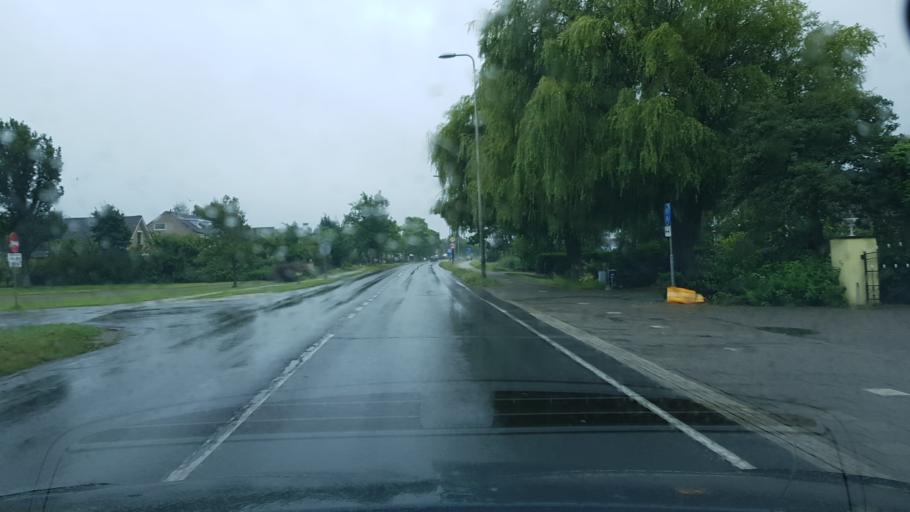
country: NL
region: South Holland
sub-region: Gemeente Katwijk
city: Rijnsburg
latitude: 52.2009
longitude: 4.4461
